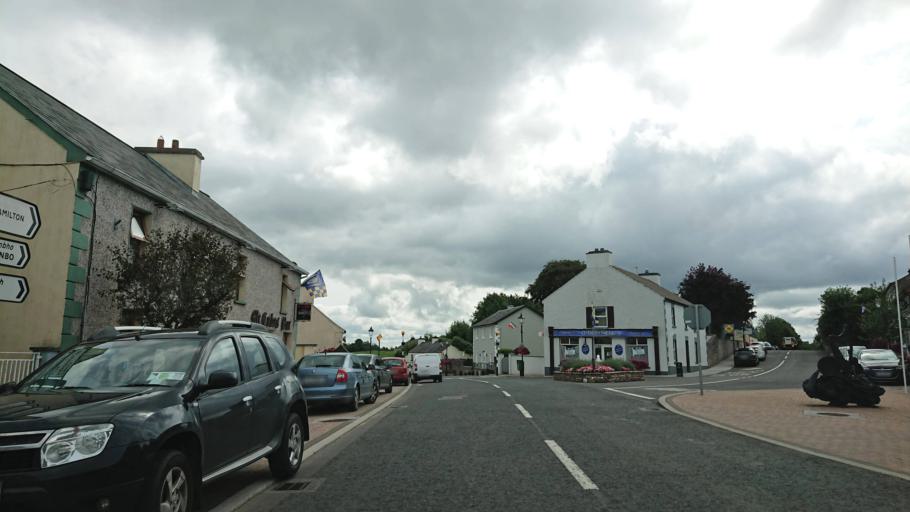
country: IE
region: Connaught
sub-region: County Leitrim
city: Carrick-on-Shannon
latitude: 54.0510
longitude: -8.1377
